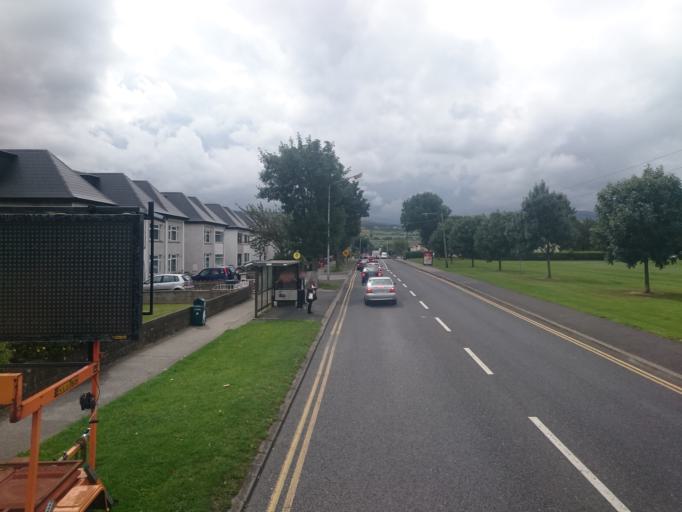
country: IE
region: Leinster
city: Oldbawn
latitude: 53.2817
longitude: -6.3591
